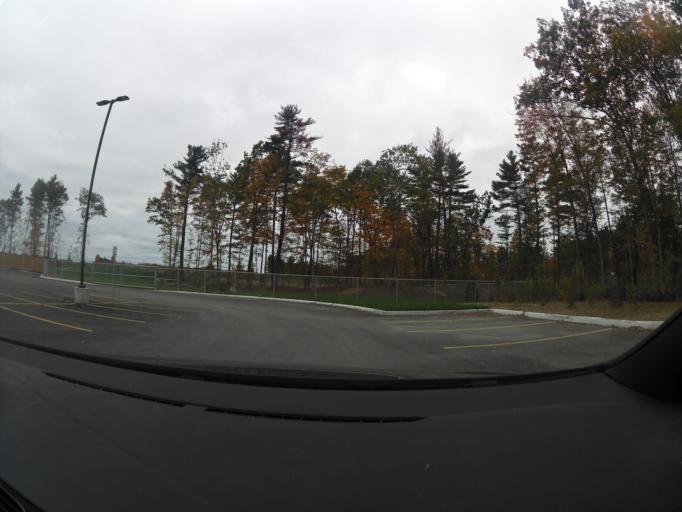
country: CA
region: Ontario
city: Bells Corners
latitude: 45.3376
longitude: -75.9419
